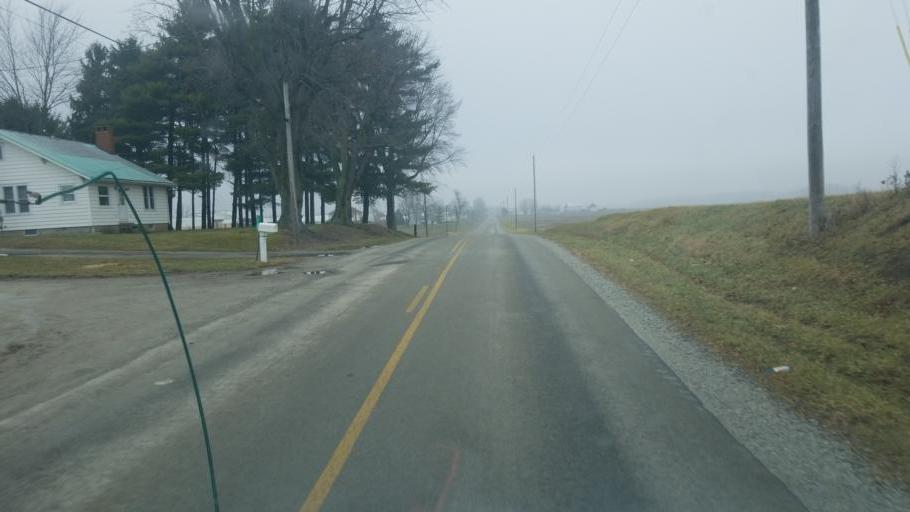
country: US
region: Ohio
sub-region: Hardin County
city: Kenton
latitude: 40.5493
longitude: -83.5134
